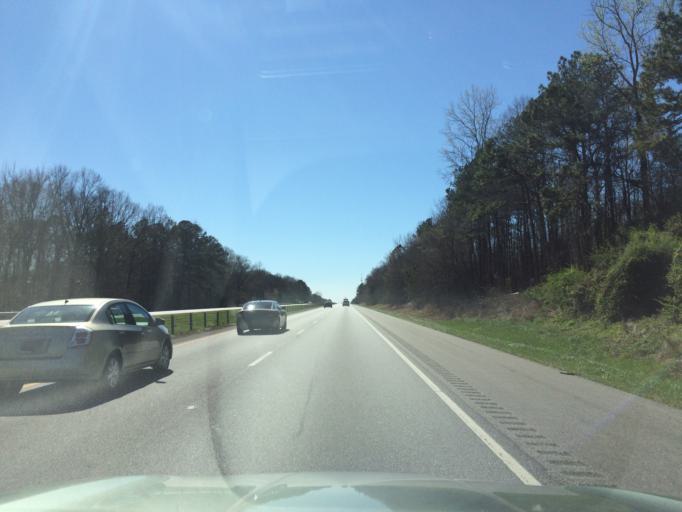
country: US
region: Alabama
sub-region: Lee County
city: Auburn
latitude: 32.5719
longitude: -85.4835
